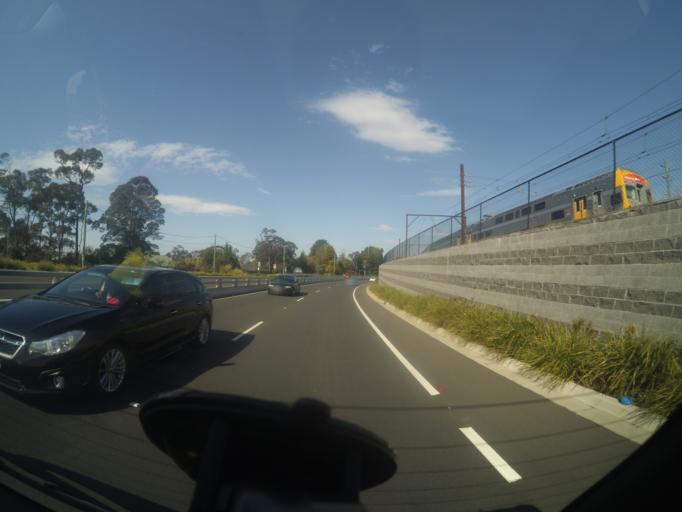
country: AU
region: New South Wales
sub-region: Blue Mountains Municipality
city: Hazelbrook
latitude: -33.7305
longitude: 150.4636
